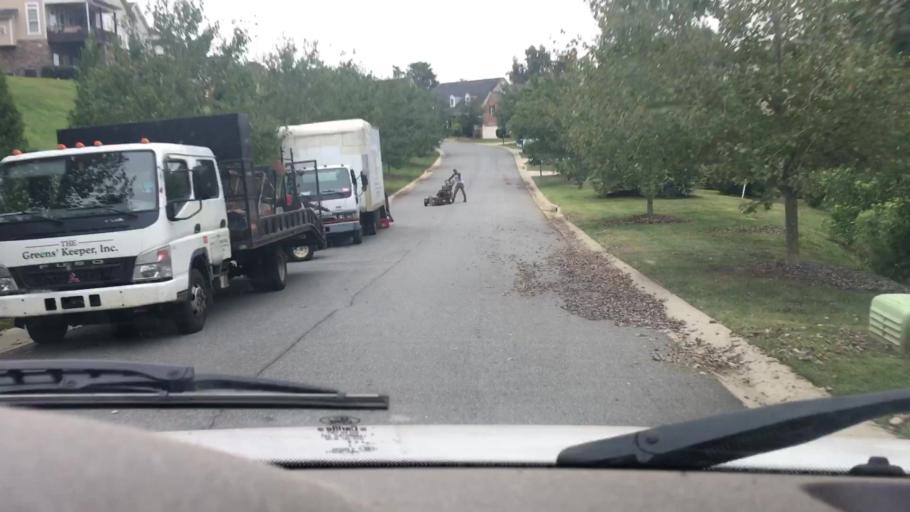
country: US
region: North Carolina
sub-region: Lincoln County
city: Denver
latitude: 35.4770
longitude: -81.0301
